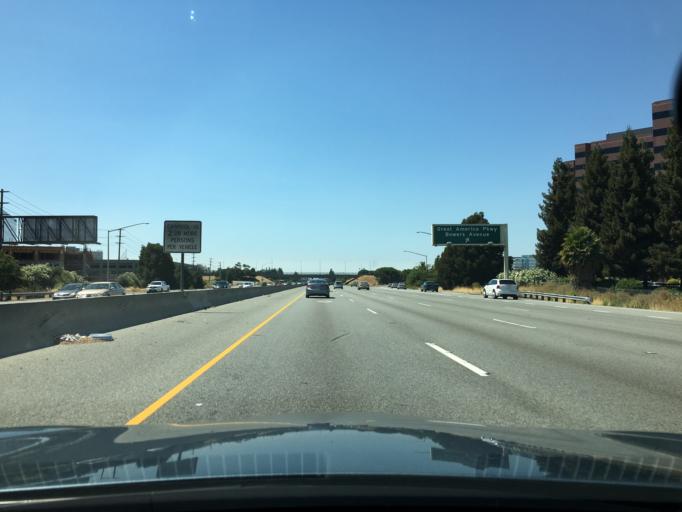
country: US
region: California
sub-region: Santa Clara County
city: Santa Clara
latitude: 37.3842
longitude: -121.9711
